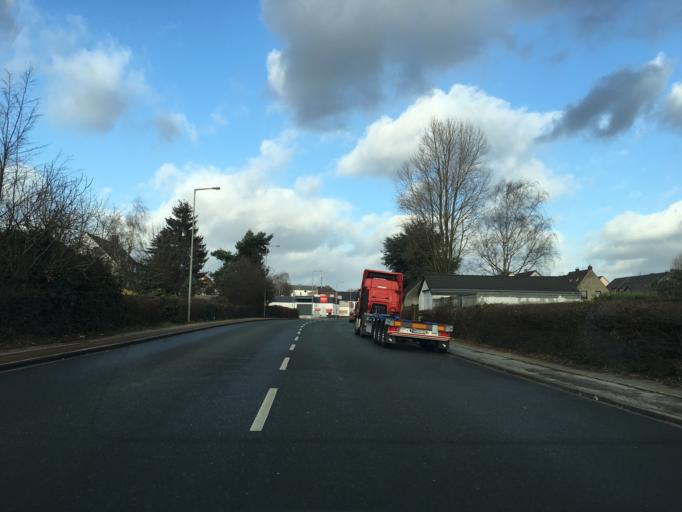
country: DE
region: North Rhine-Westphalia
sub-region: Regierungsbezirk Dusseldorf
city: Oberhausen
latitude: 51.5078
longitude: 6.8360
